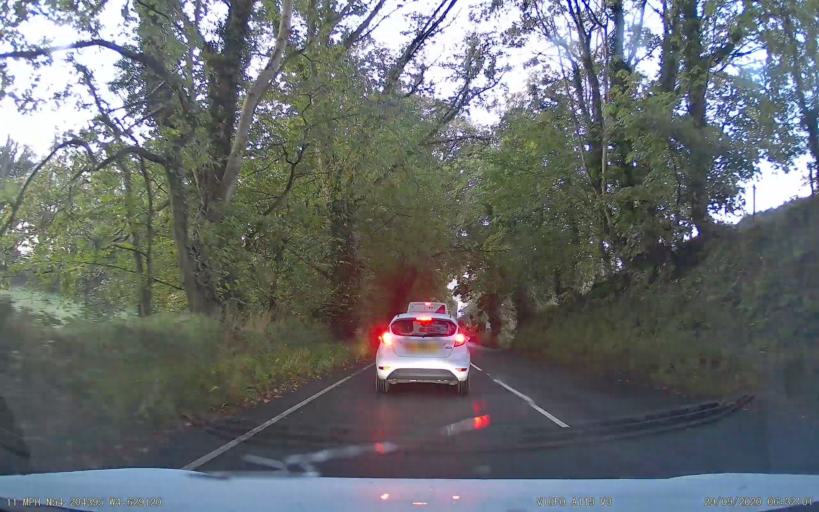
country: IM
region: Castletown
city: Castletown
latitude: 54.2044
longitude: -4.6297
